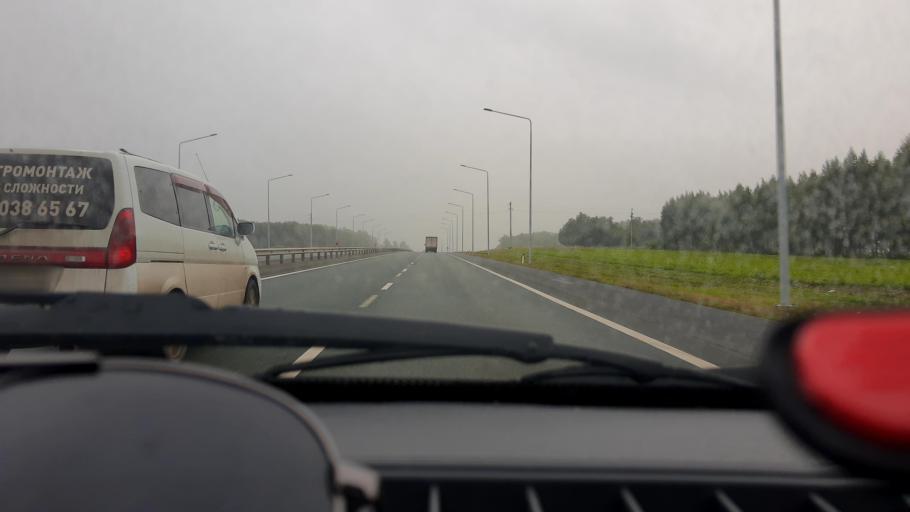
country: RU
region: Bashkortostan
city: Tolbazy
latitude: 53.9793
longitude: 55.9207
